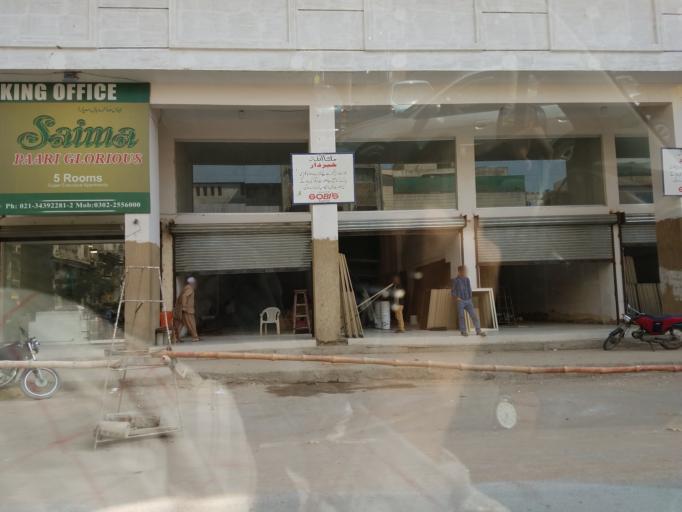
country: PK
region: Sindh
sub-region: Karachi District
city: Karachi
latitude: 24.8779
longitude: 67.0638
